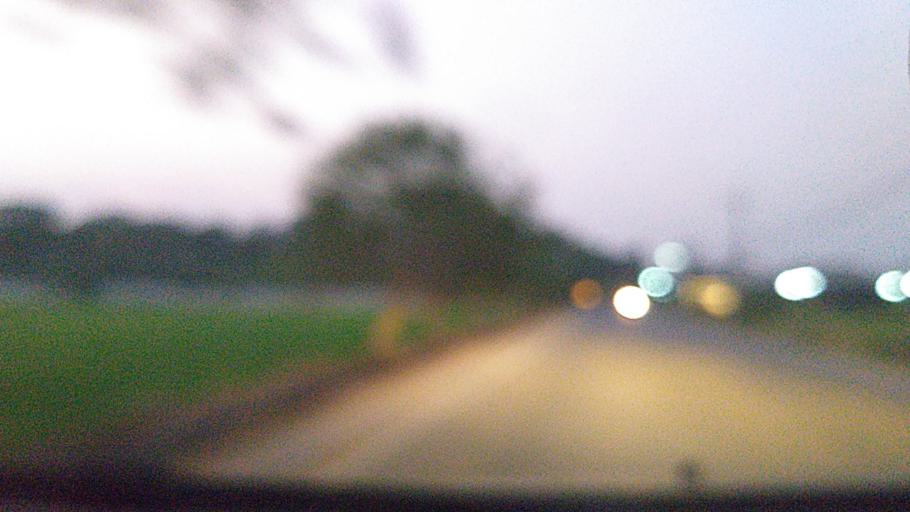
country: TH
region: Sing Buri
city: Sing Buri
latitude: 14.8479
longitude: 100.3911
